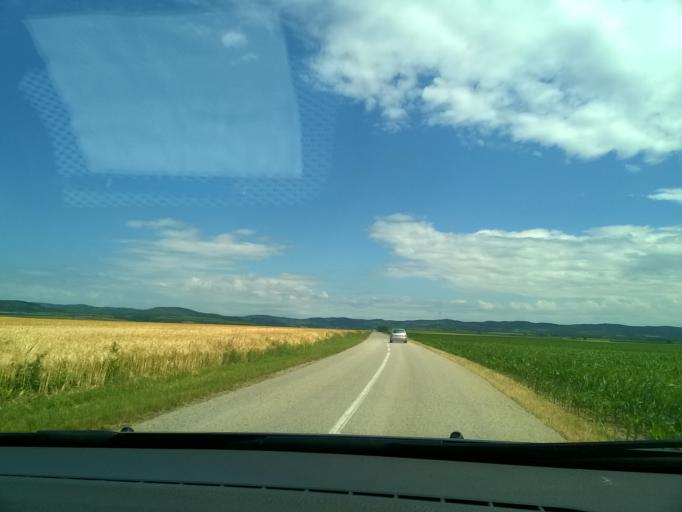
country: RS
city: Vrdnik
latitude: 45.0722
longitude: 19.8093
